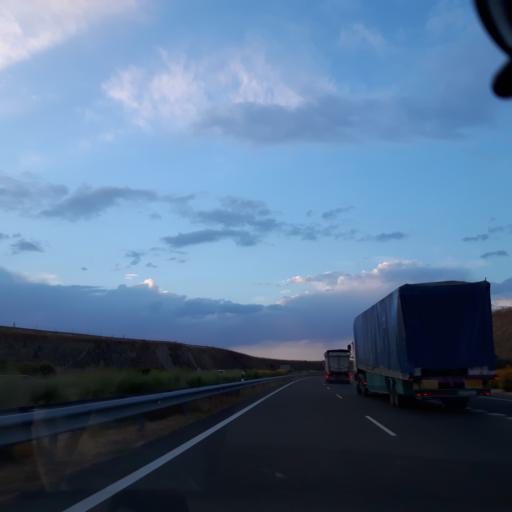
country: ES
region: Castille and Leon
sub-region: Provincia de Salamanca
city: Mozarbez
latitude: 40.8662
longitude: -5.6496
